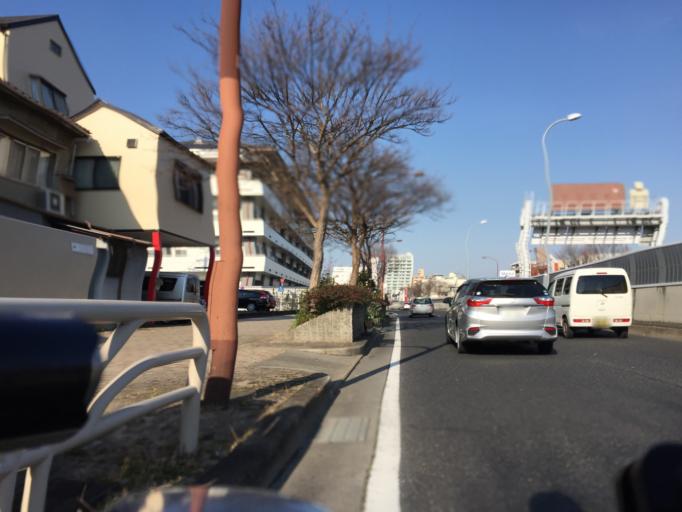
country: JP
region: Aichi
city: Nagoya-shi
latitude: 35.1590
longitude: 136.9410
